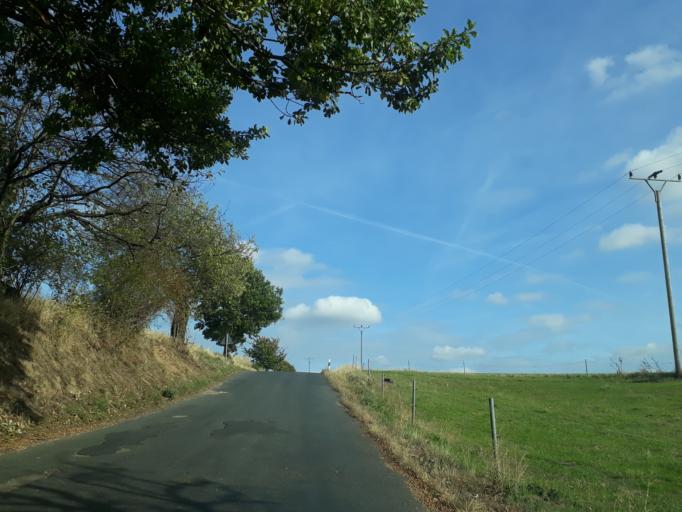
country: DE
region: Saxony
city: Klipphausen
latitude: 51.0855
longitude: 13.5714
